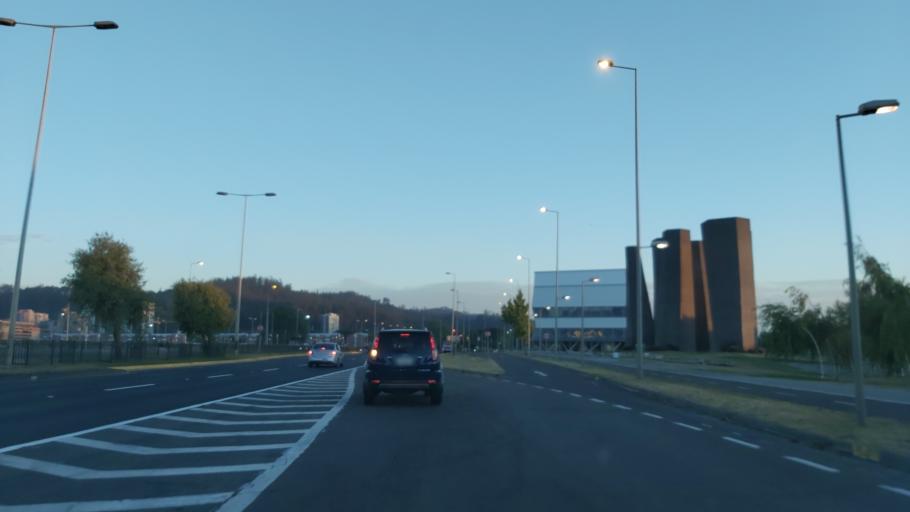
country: CL
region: Biobio
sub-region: Provincia de Concepcion
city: Concepcion
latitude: -36.8310
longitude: -73.0668
